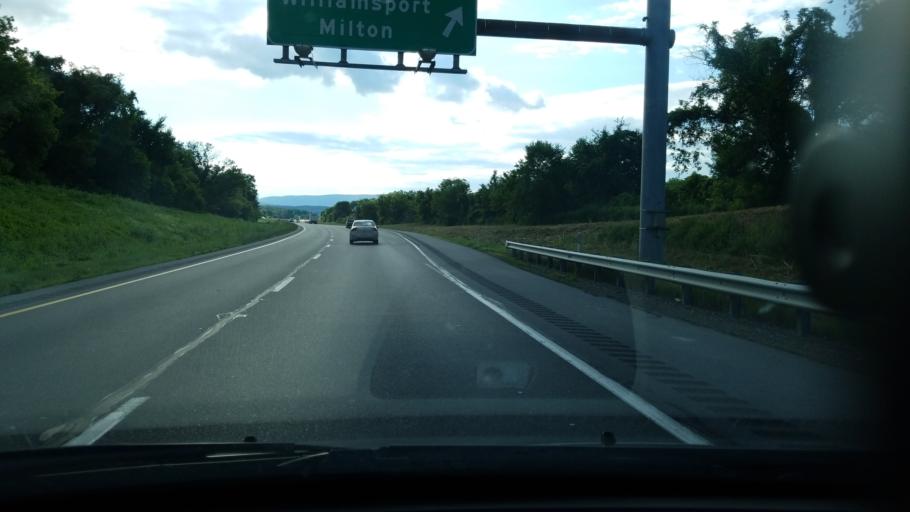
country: US
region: Pennsylvania
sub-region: Northumberland County
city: Milton
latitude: 41.0468
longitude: -76.8251
